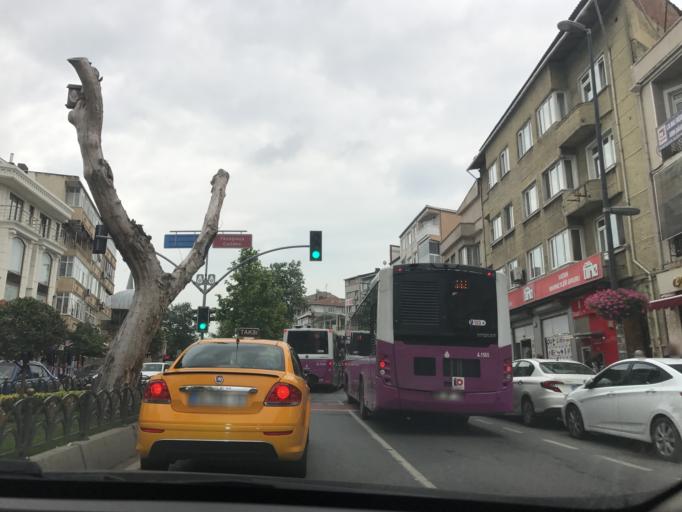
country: TR
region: Istanbul
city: Istanbul
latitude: 41.0260
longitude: 28.9398
